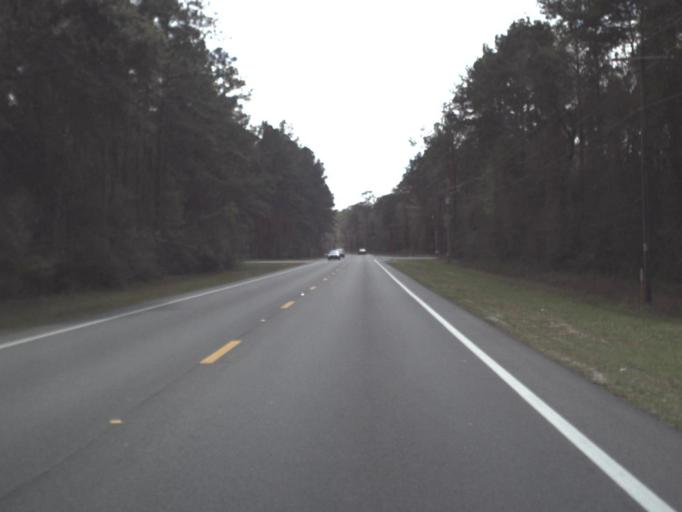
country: US
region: Florida
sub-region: Leon County
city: Woodville
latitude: 30.2998
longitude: -84.3481
